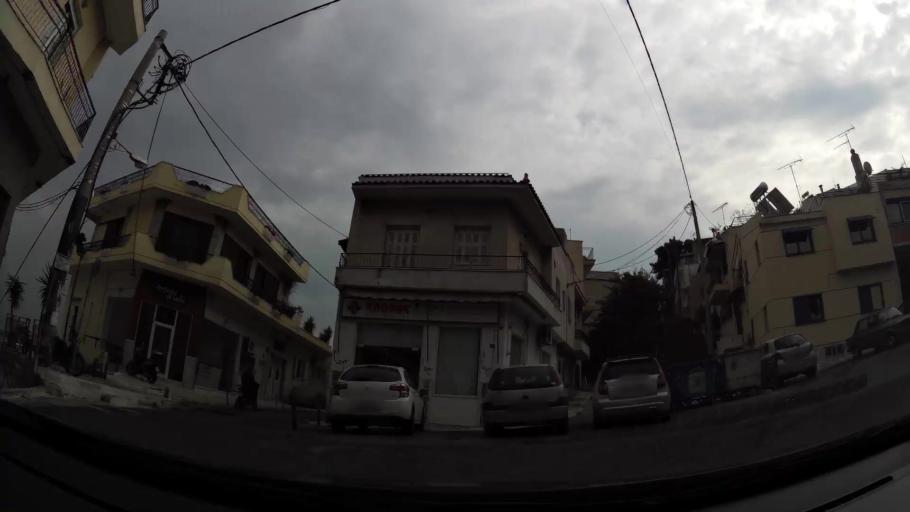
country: GR
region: Attica
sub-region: Nomos Attikis
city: Piraeus
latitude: 37.9422
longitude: 23.6555
